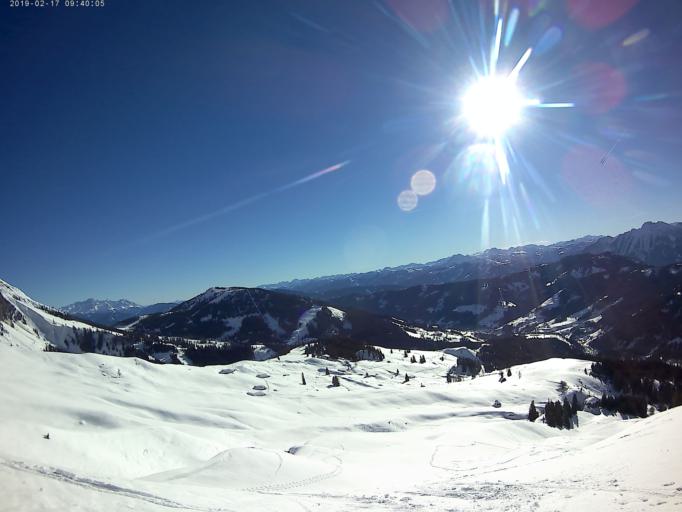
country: AT
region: Salzburg
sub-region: Politischer Bezirk Sankt Johann im Pongau
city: Muhlbach am Hochkonig
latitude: 47.4060
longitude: 13.0820
